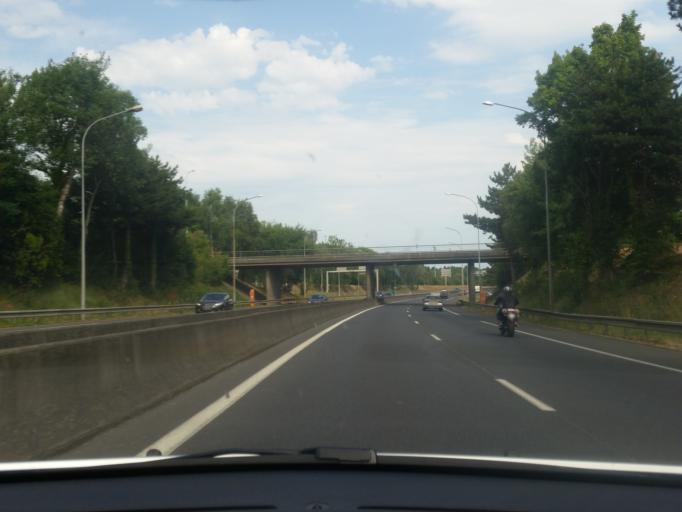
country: FR
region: Pays de la Loire
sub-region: Departement de Maine-et-Loire
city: Avrille
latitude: 47.4694
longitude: -0.5903
